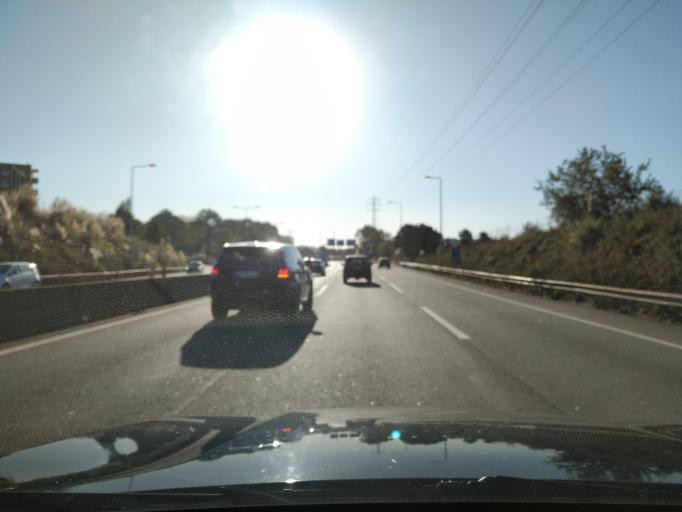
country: PT
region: Porto
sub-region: Vila Nova de Gaia
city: Canidelo
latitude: 41.1182
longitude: -8.6329
